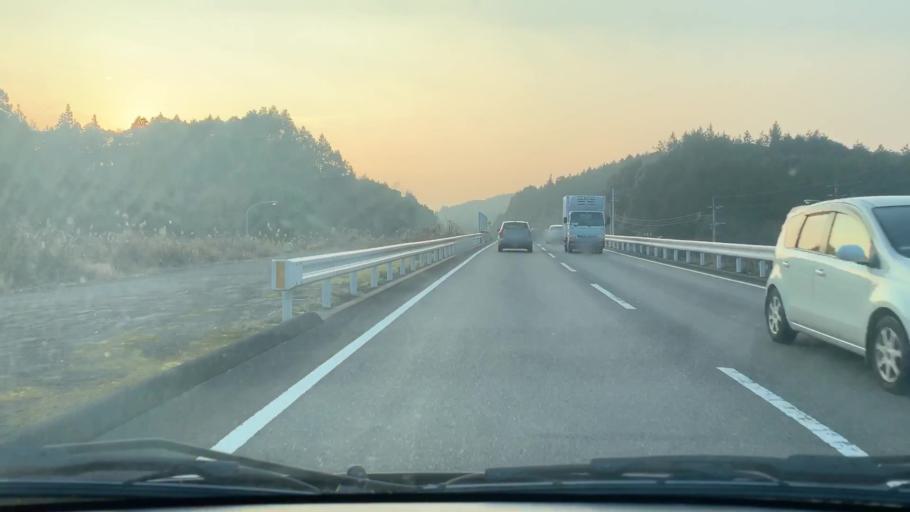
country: JP
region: Saga Prefecture
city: Imaricho-ko
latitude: 33.2636
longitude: 129.9441
